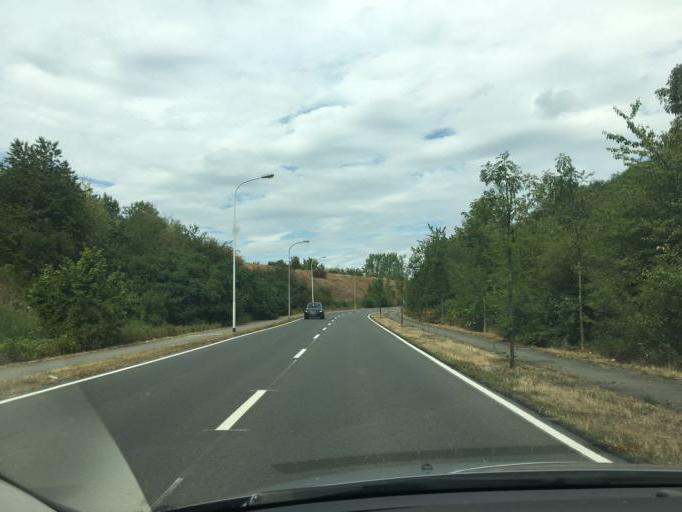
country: DE
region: Saxony-Anhalt
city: Angersdorf
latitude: 51.4369
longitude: 11.9460
